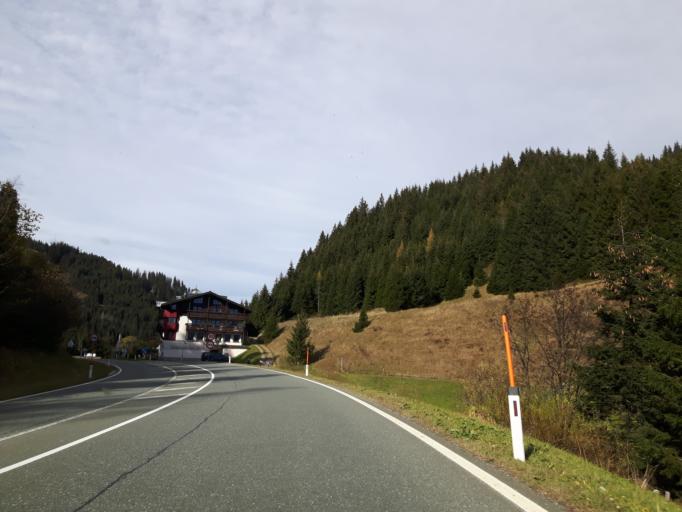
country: AT
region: Salzburg
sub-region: Politischer Bezirk Zell am See
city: Hollersbach im Pinzgau
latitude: 47.3082
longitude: 12.4099
